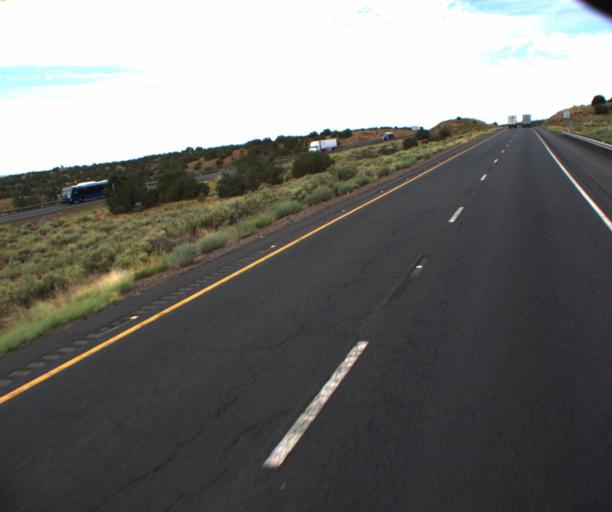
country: US
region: Arizona
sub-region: Apache County
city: Houck
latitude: 35.2795
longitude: -109.2494
